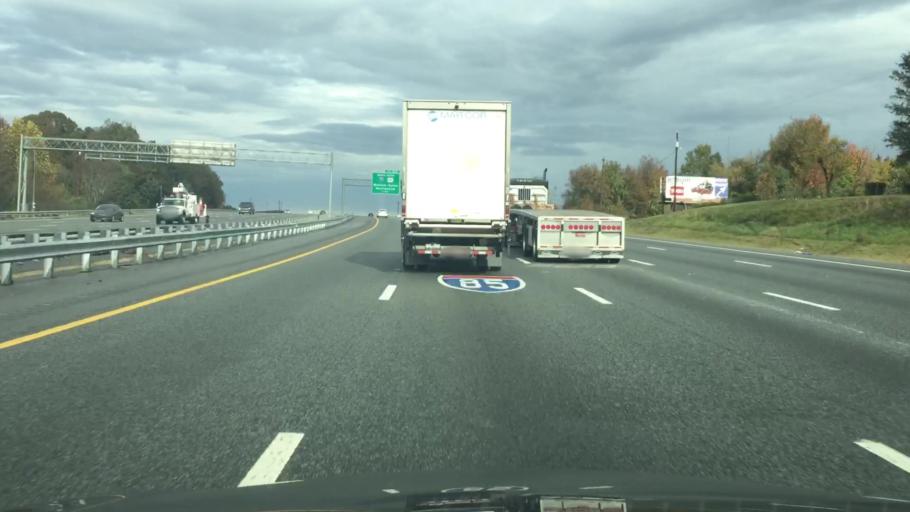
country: US
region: North Carolina
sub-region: Guilford County
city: Jamestown
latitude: 35.9937
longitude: -79.8698
